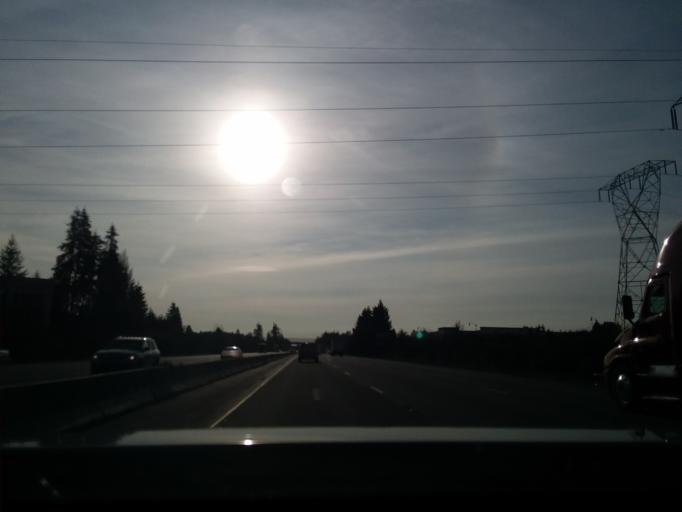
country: US
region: Washington
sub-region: Thurston County
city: Tumwater
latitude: 46.9927
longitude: -122.9170
